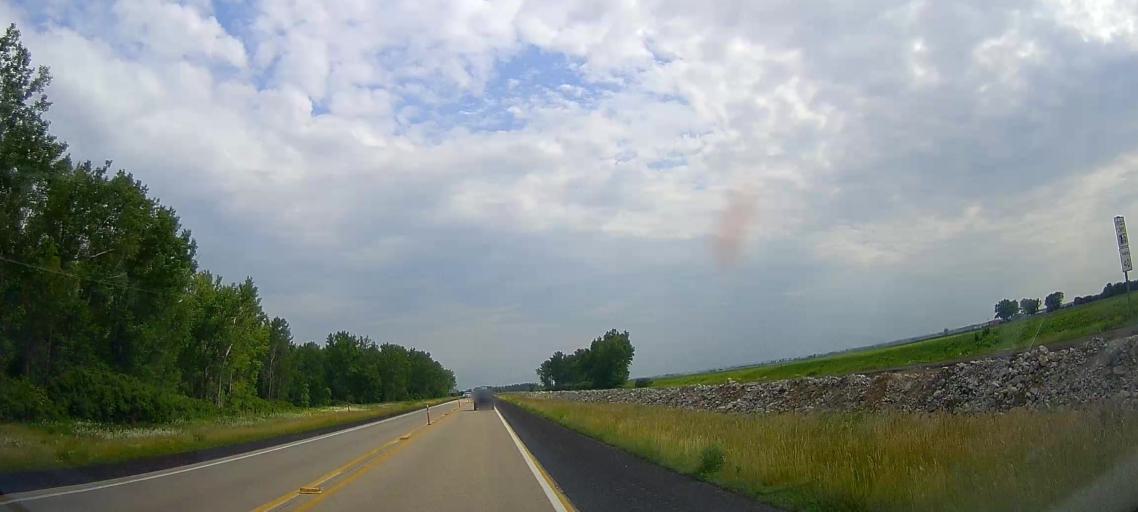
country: US
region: Nebraska
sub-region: Washington County
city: Blair
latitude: 41.7012
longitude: -96.0429
